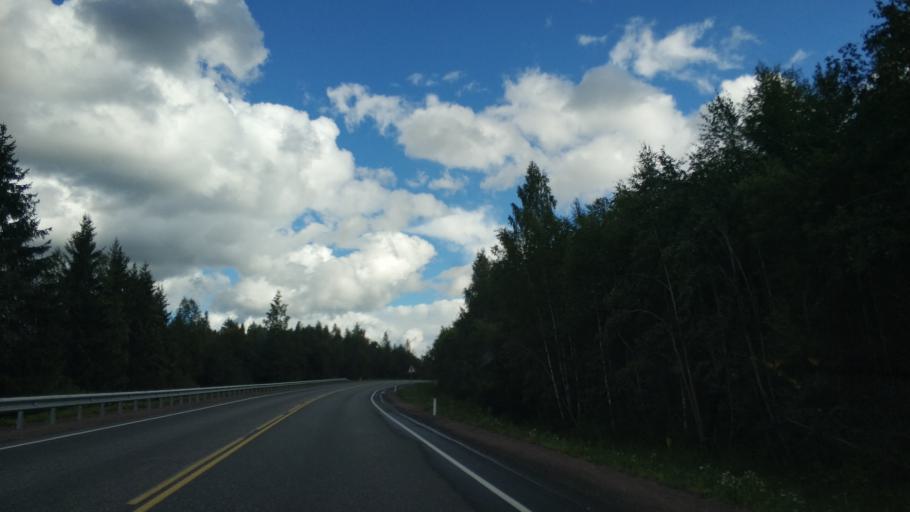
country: RU
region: Republic of Karelia
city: Khelyulya
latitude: 61.7851
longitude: 30.6470
